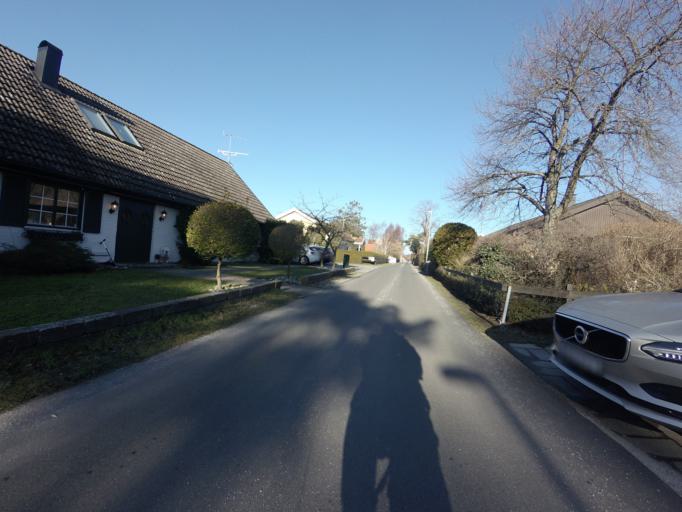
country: SE
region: Skane
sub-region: Vellinge Kommun
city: Hollviken
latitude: 55.4175
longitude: 12.9568
